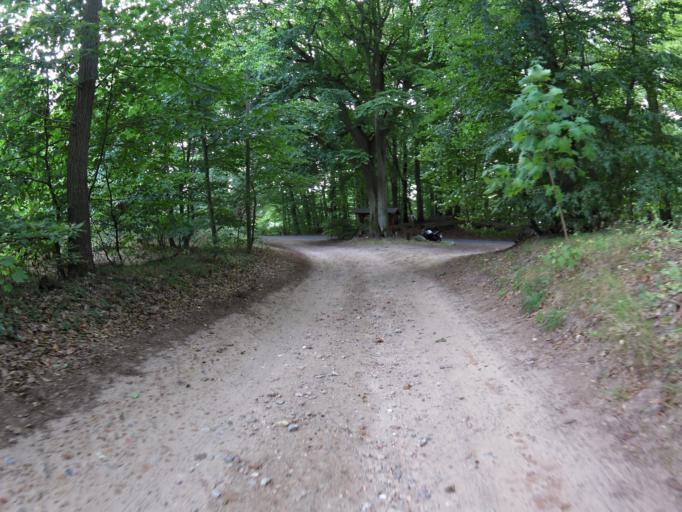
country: DE
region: Mecklenburg-Vorpommern
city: Seebad Bansin
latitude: 53.9591
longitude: 14.1081
